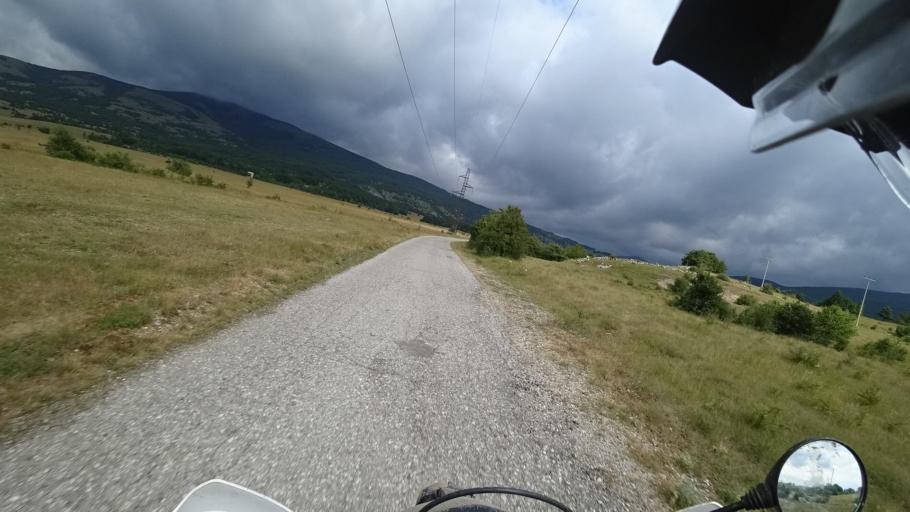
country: HR
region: Zadarska
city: Gracac
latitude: 44.5308
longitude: 15.8339
